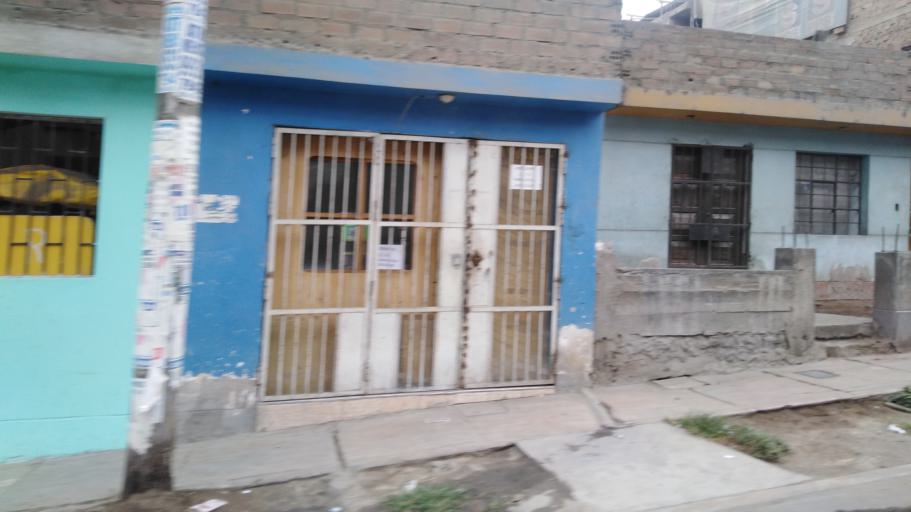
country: PE
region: Lima
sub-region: Lima
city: La Molina
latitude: -12.1432
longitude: -76.9448
